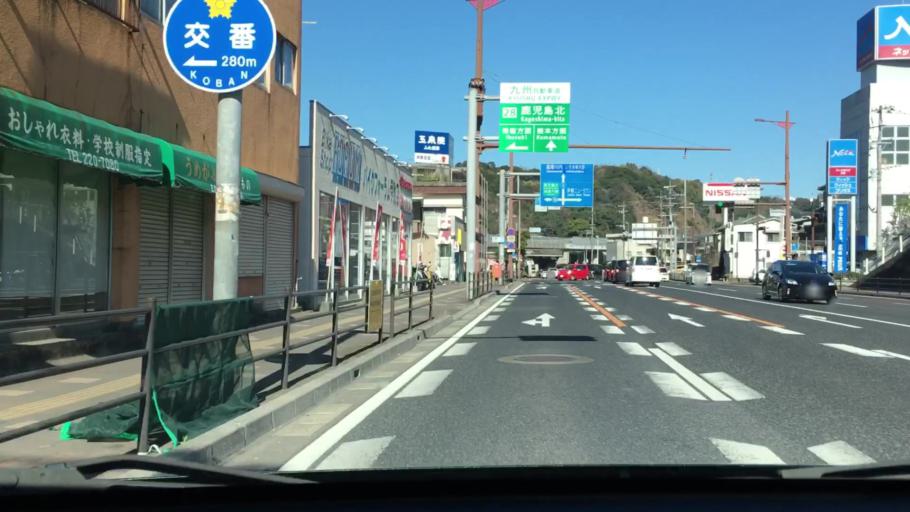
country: JP
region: Kagoshima
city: Kagoshima-shi
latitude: 31.6217
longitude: 130.5264
